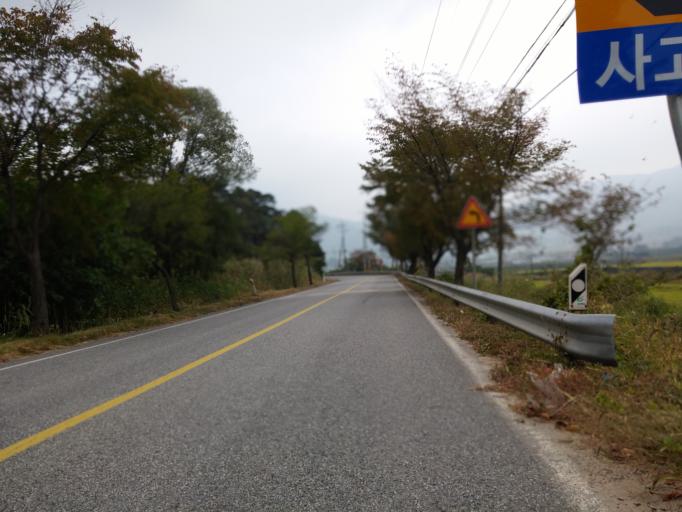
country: KR
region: Chungcheongbuk-do
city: Okcheon
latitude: 36.3932
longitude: 127.7234
